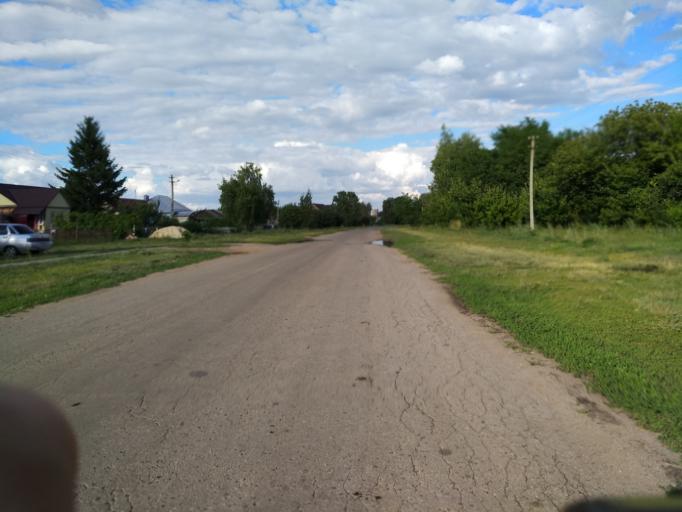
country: RU
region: Lipetsk
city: Dobrinka
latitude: 52.0379
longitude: 40.5318
